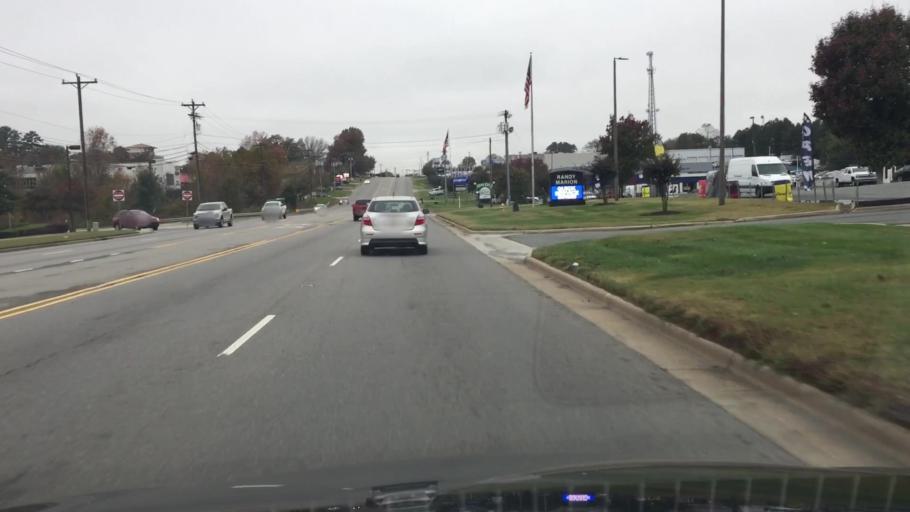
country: US
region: North Carolina
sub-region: Iredell County
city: Mooresville
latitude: 35.5899
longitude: -80.8417
